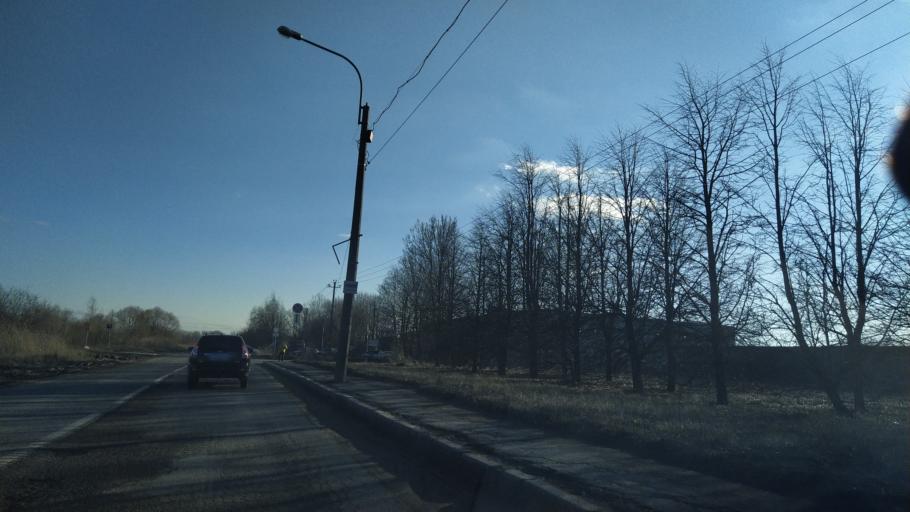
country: RU
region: St.-Petersburg
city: Pushkin
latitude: 59.6959
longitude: 30.3955
